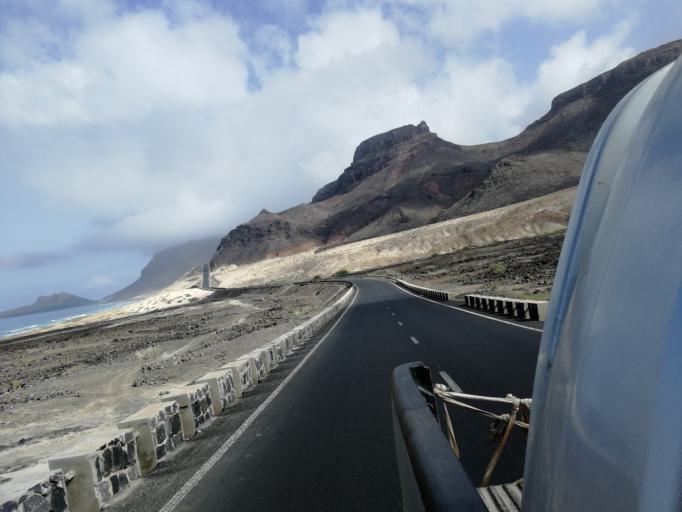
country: CV
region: Sao Vicente
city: Mindelo
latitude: 16.8745
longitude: -24.9094
